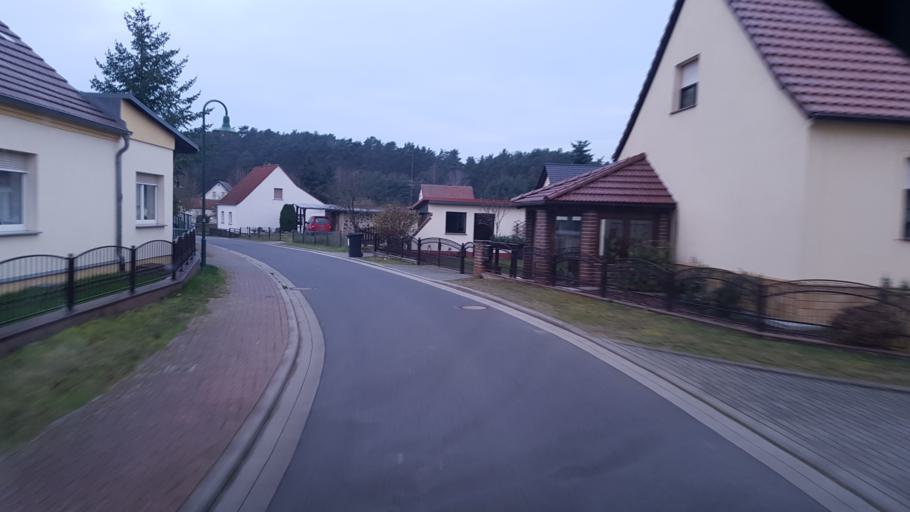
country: DE
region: Brandenburg
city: Gross Lindow
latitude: 52.1103
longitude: 14.4932
